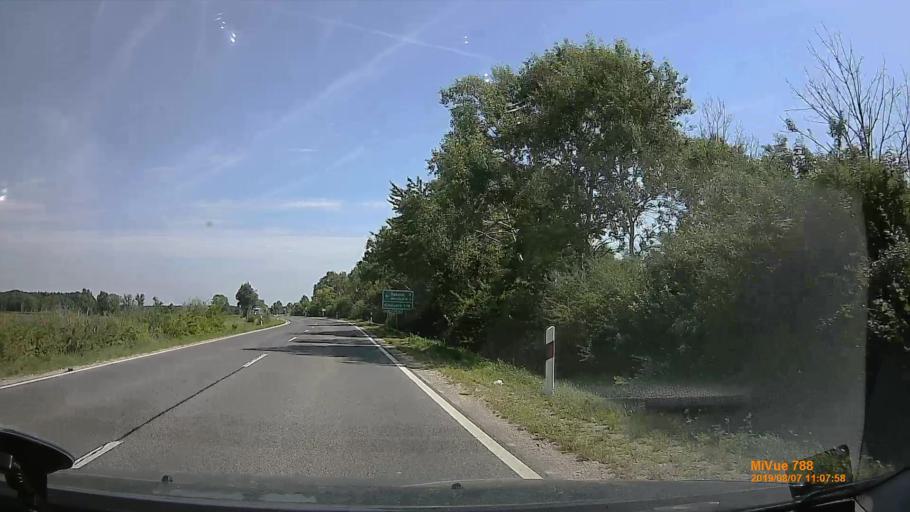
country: HU
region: Zala
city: Lenti
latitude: 46.6296
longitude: 16.4731
